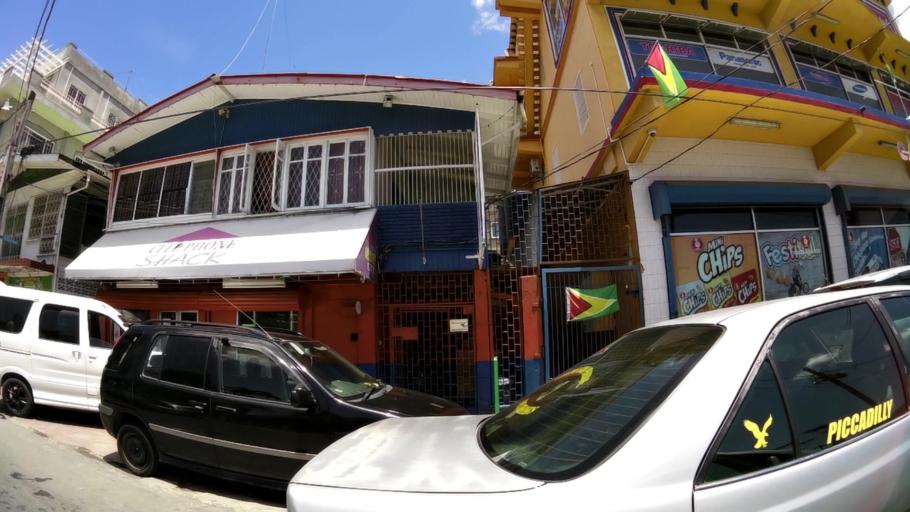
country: GY
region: Demerara-Mahaica
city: Georgetown
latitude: 6.8117
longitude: -58.1601
